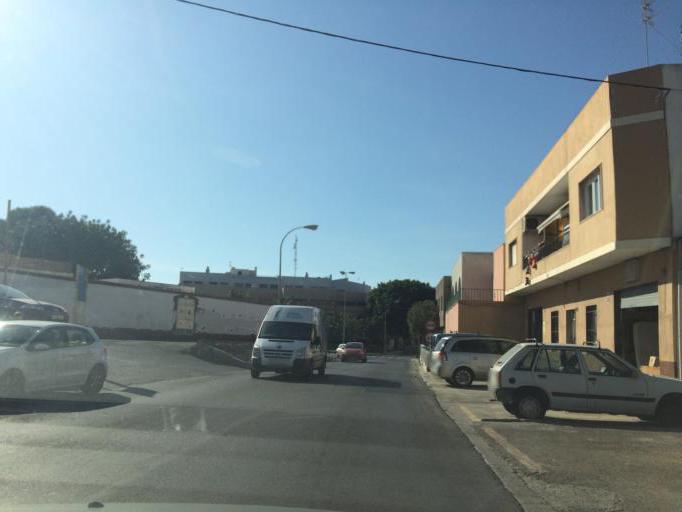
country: ES
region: Andalusia
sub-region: Provincia de Almeria
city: Almeria
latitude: 36.8392
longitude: -2.4422
